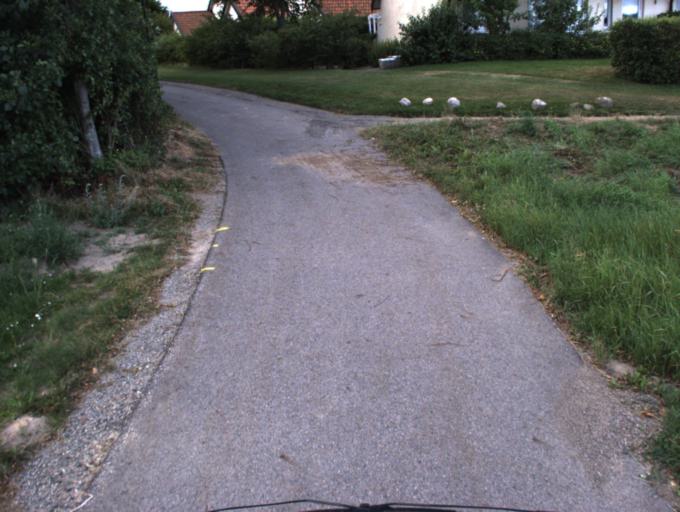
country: SE
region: Skane
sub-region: Helsingborg
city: Helsingborg
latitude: 56.0985
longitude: 12.6509
